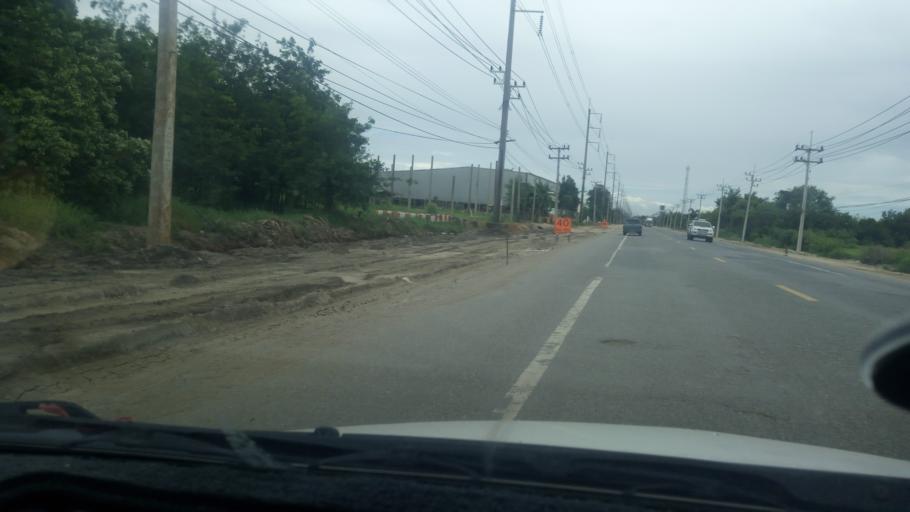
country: TH
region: Chon Buri
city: Phan Thong
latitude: 13.5194
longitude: 101.1544
